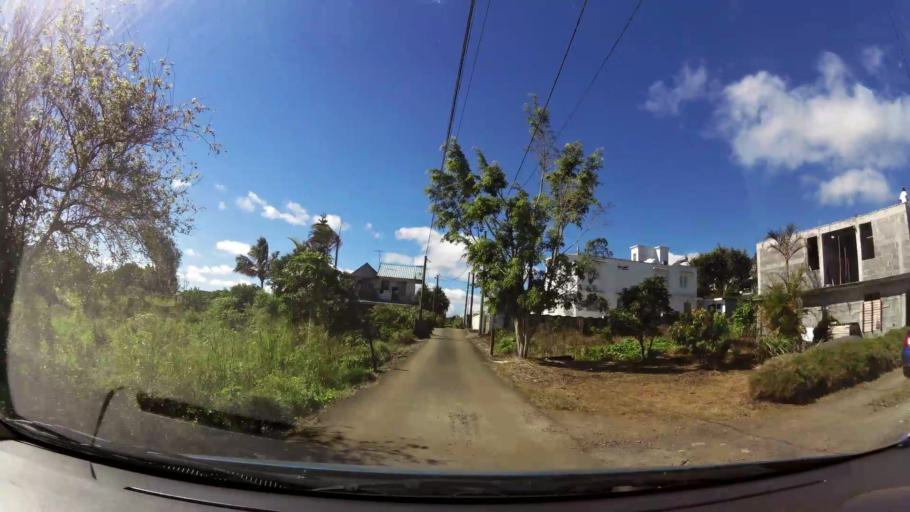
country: MU
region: Plaines Wilhems
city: Curepipe
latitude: -20.3428
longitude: 57.4943
